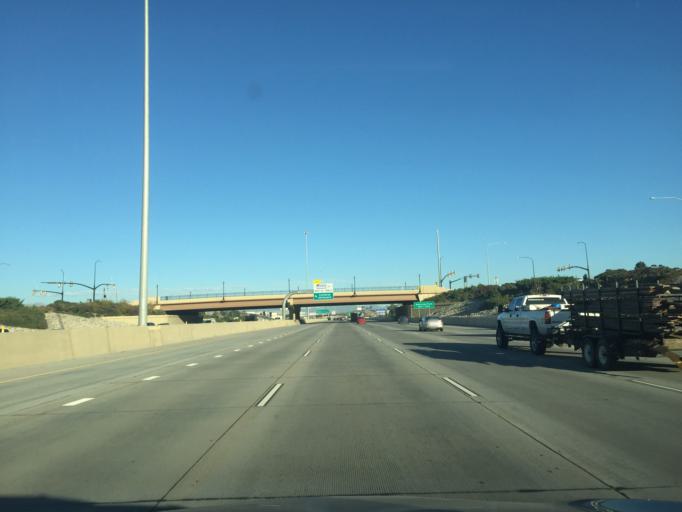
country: US
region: Utah
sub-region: Utah County
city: Pleasant Grove
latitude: 40.3489
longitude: -111.7670
